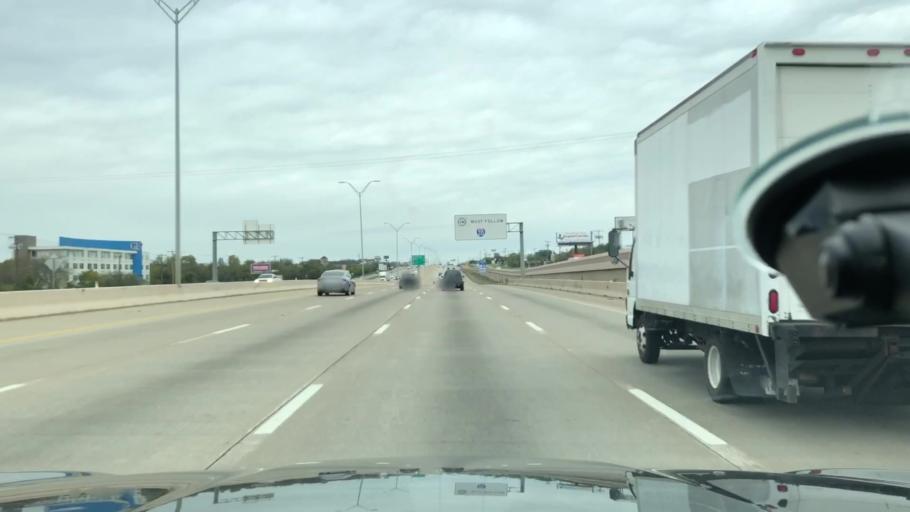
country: US
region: Texas
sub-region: Dallas County
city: DeSoto
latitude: 32.6096
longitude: -96.8229
